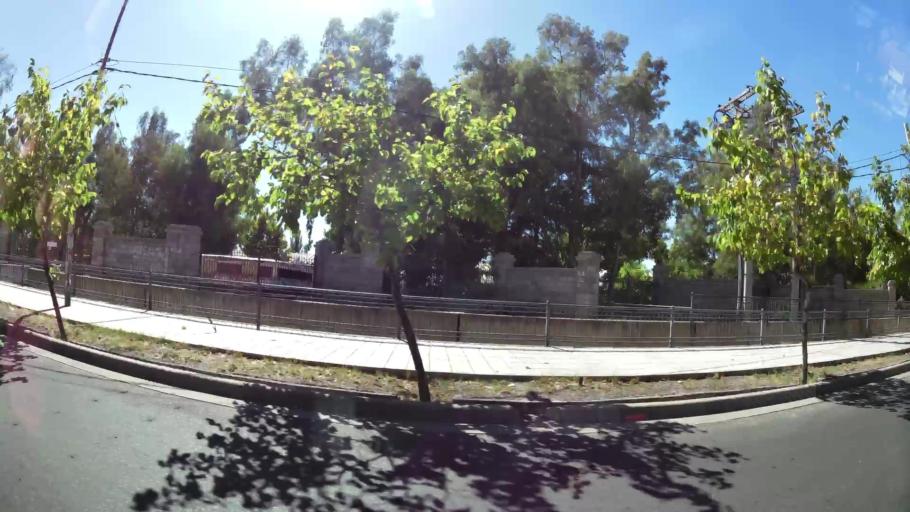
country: AR
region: Mendoza
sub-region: Departamento de Godoy Cruz
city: Godoy Cruz
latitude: -32.9127
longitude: -68.8700
